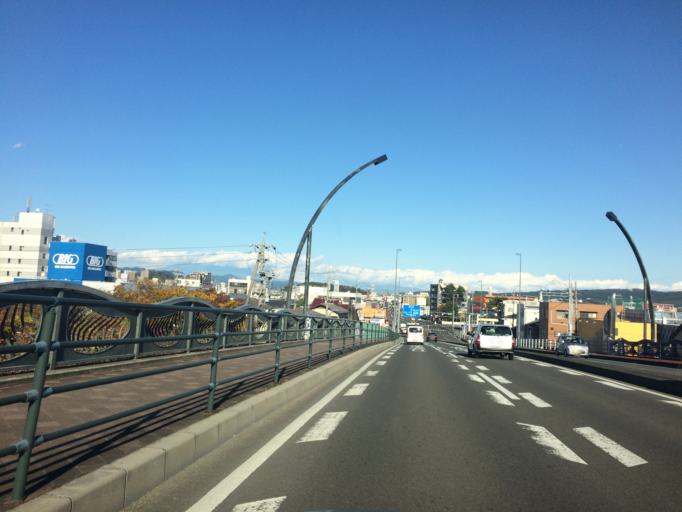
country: JP
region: Shizuoka
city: Shizuoka-shi
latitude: 34.9536
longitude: 138.3805
